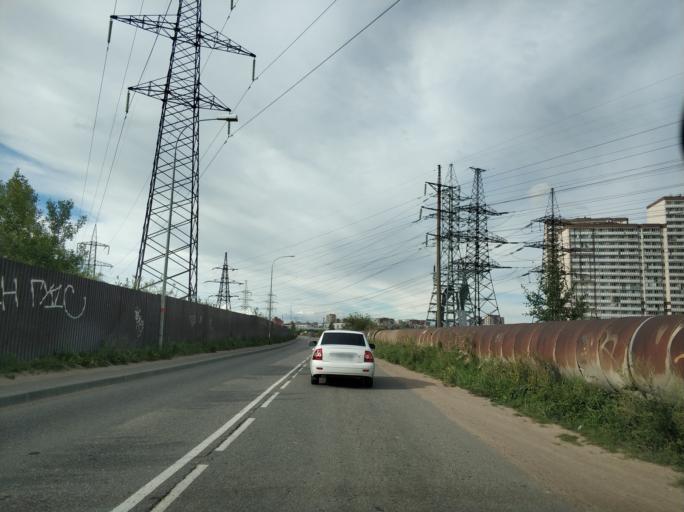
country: RU
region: Leningrad
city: Murino
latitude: 60.0491
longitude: 30.4402
